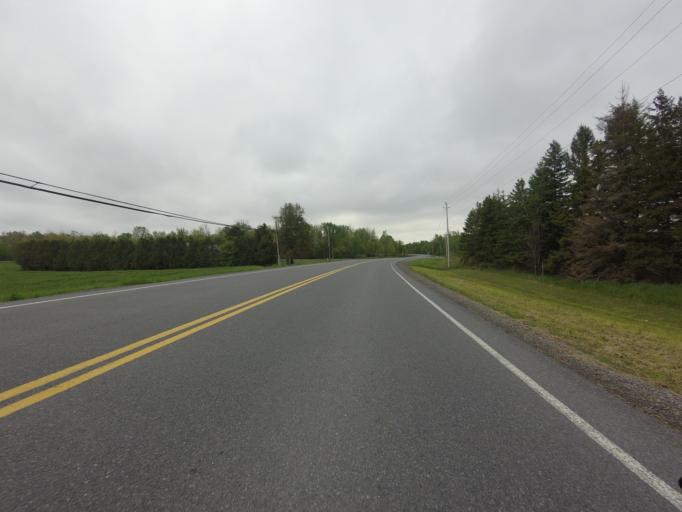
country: CA
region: Ontario
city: Casselman
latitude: 45.1333
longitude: -75.2480
